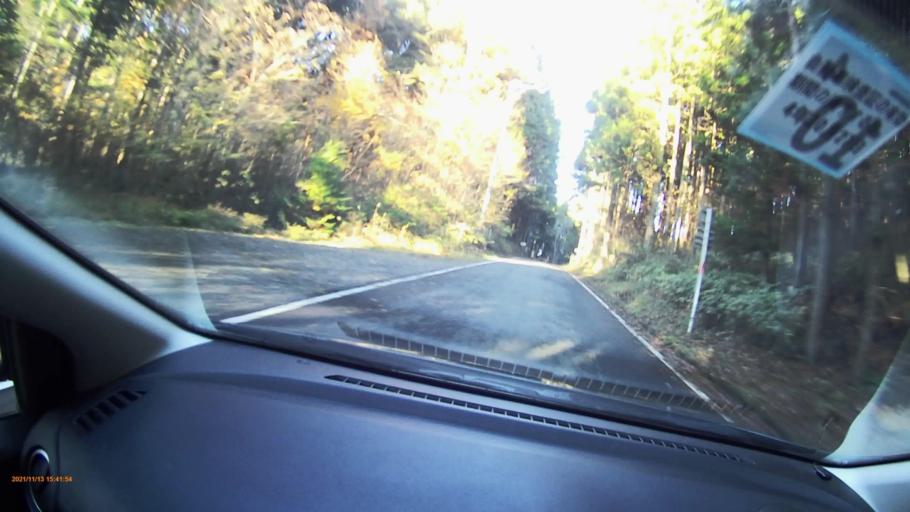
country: JP
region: Gifu
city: Nakatsugawa
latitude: 35.5895
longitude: 137.3904
